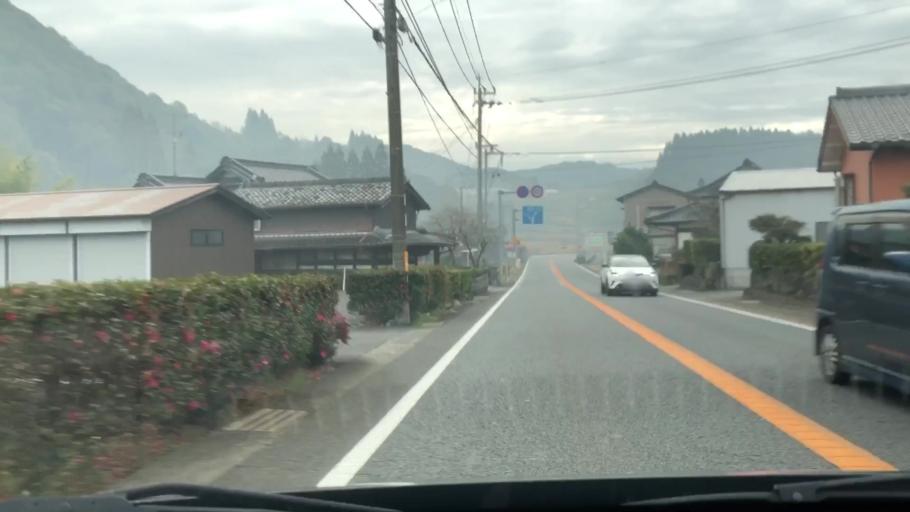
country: JP
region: Oita
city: Usuki
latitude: 33.0184
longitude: 131.6999
